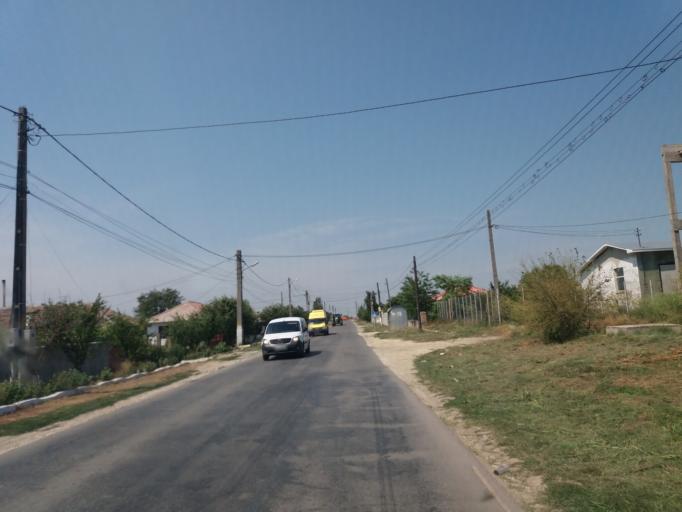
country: RO
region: Constanta
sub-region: Comuna Corbu
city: Corbu
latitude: 44.4027
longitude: 28.6616
